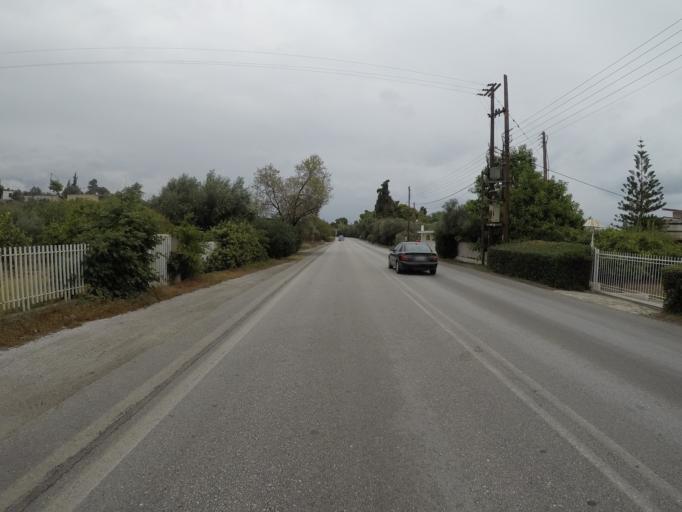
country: GR
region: Peloponnese
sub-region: Nomos Korinthias
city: Agioi Theodoroi
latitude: 37.9181
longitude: 23.1157
